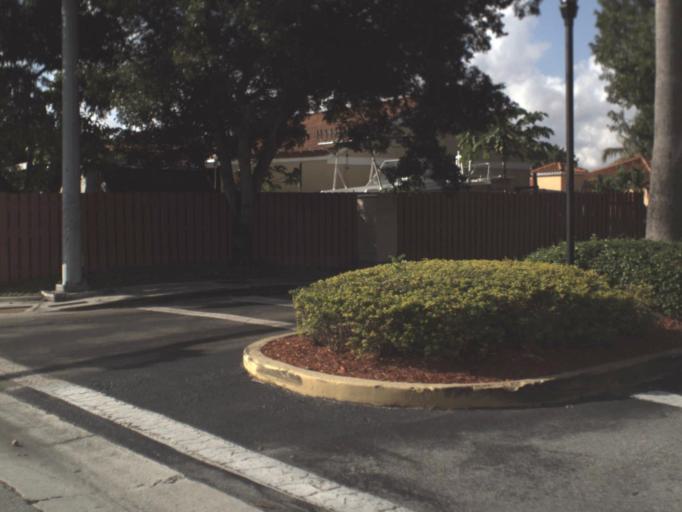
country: US
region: Florida
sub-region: Miami-Dade County
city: Three Lakes
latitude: 25.6268
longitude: -80.4000
